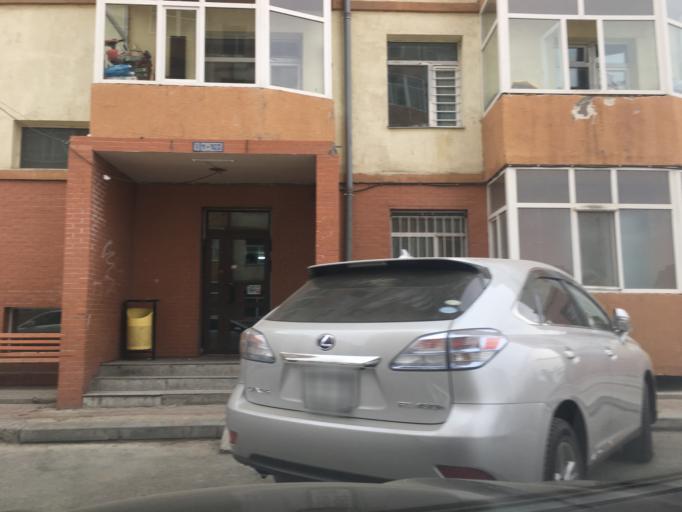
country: MN
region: Ulaanbaatar
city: Ulaanbaatar
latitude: 47.9037
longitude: 106.8865
